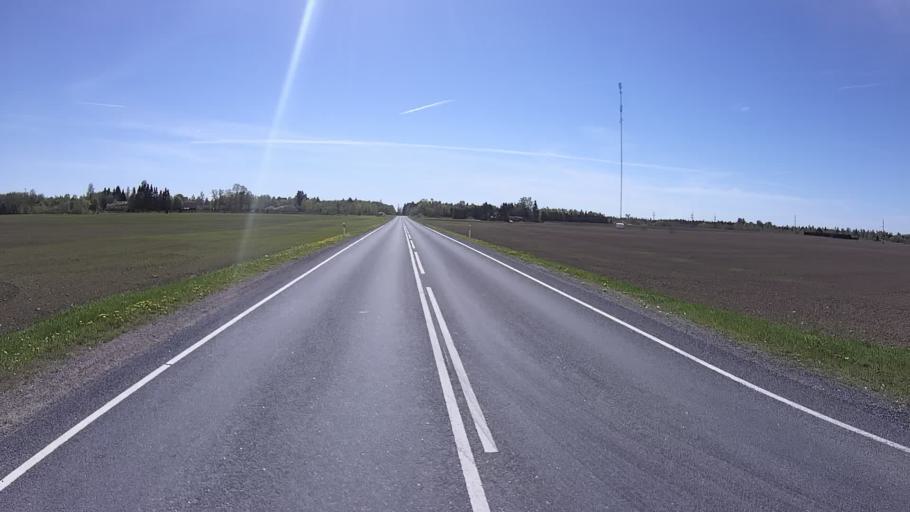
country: EE
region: Harju
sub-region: Anija vald
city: Kehra
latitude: 59.3497
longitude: 25.3186
